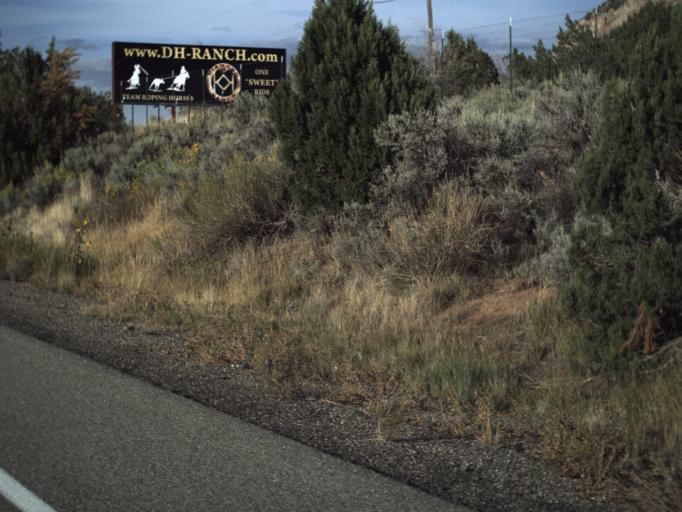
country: US
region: Utah
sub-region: Washington County
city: Toquerville
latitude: 37.4849
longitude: -113.2196
